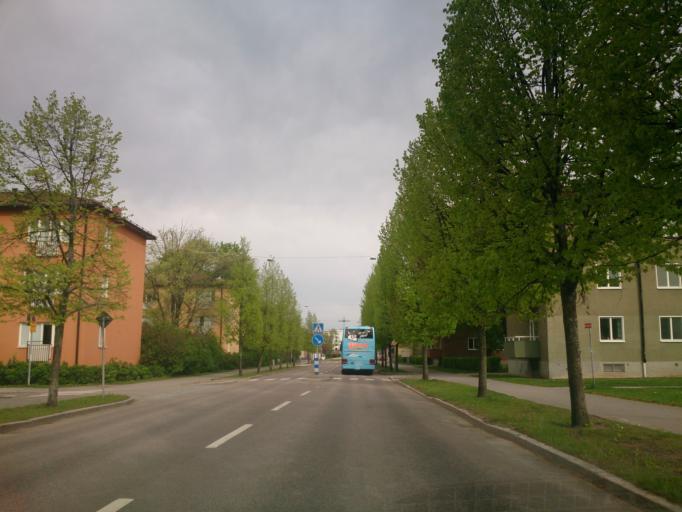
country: SE
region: OEstergoetland
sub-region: Linkopings Kommun
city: Linkoping
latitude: 58.4091
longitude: 15.6379
